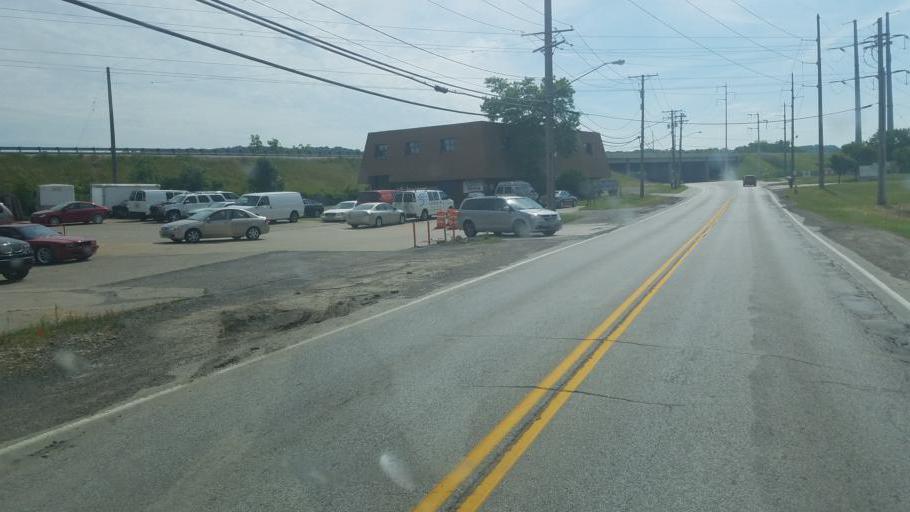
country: US
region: Ohio
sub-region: Cuyahoga County
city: North Royalton
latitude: 41.3132
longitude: -81.7598
